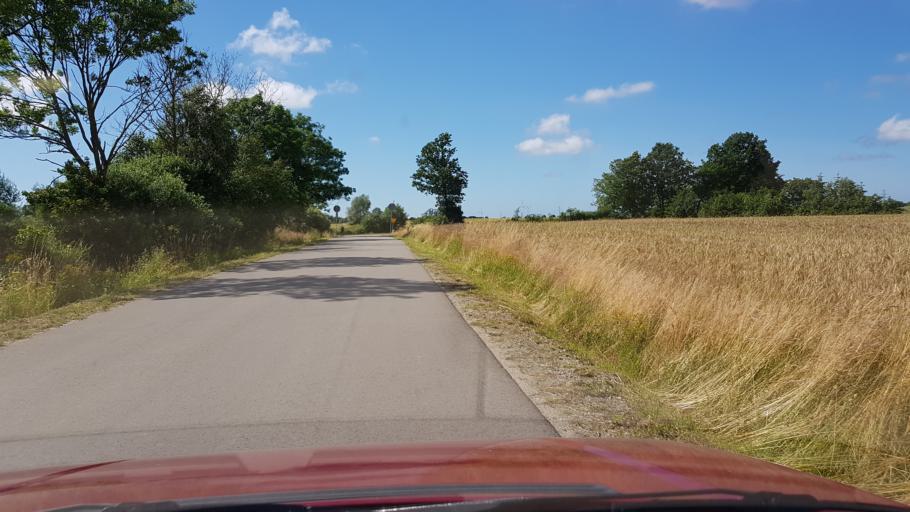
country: PL
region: West Pomeranian Voivodeship
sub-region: Powiat bialogardzki
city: Karlino
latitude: 54.1676
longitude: 15.9203
